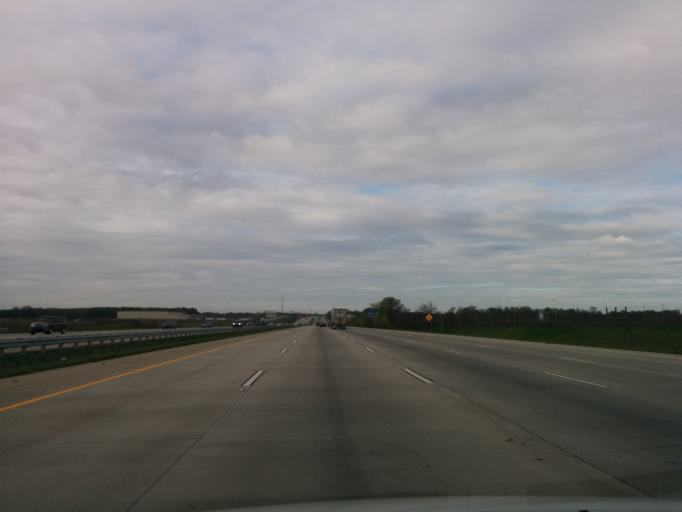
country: US
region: Georgia
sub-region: Peach County
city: Byron
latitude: 32.7198
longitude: -83.7285
